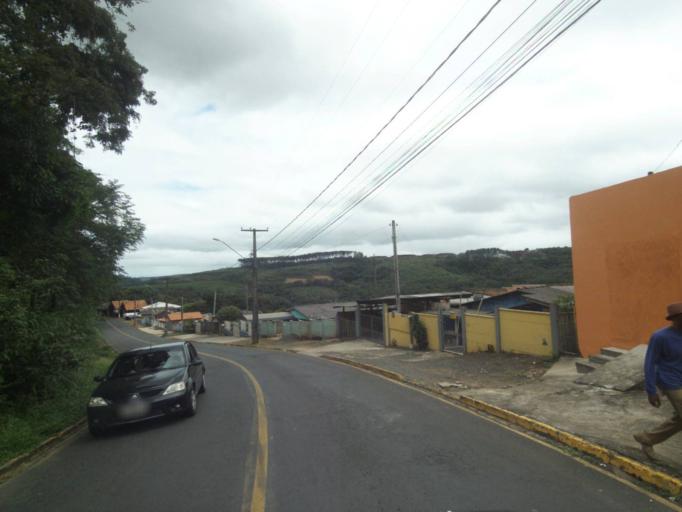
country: BR
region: Parana
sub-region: Telemaco Borba
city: Telemaco Borba
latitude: -24.3162
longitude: -50.6163
